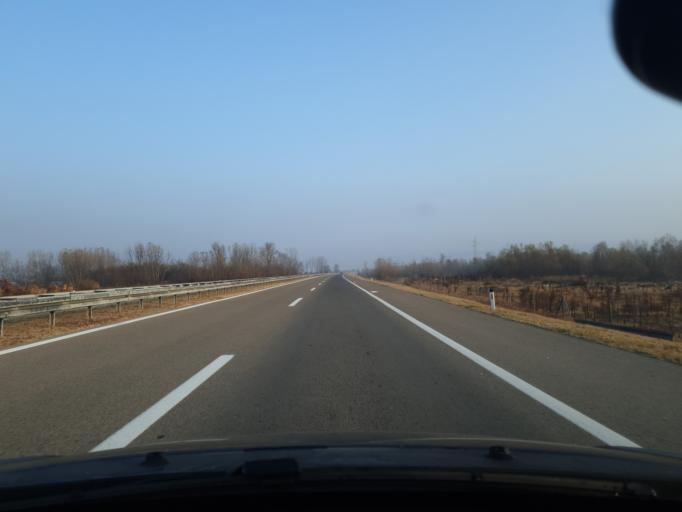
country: RS
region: Central Serbia
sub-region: Jablanicki Okrug
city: Leskovac
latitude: 42.9463
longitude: 22.0326
